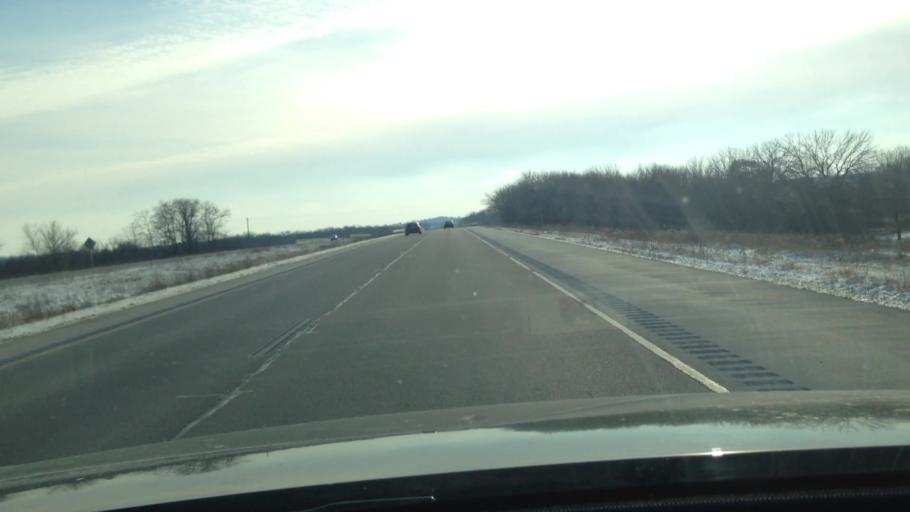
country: US
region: Wisconsin
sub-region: Walworth County
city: East Troy
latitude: 42.7950
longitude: -88.3841
